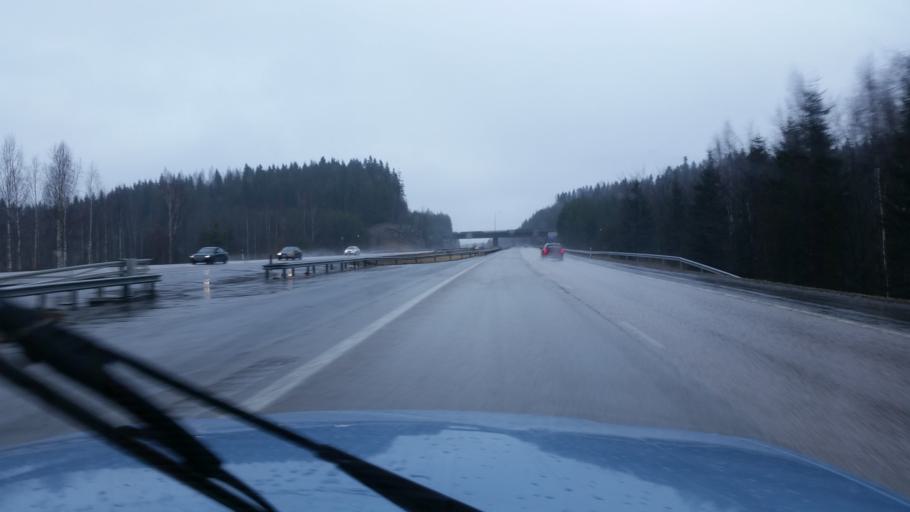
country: FI
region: Haeme
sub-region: Riihimaeki
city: Riihimaeki
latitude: 60.7408
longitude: 24.7278
